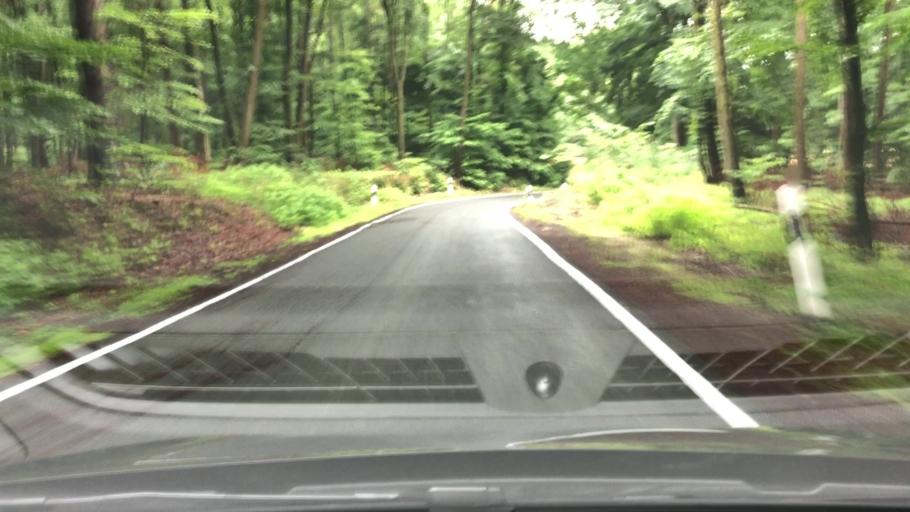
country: DE
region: North Rhine-Westphalia
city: Porta Westfalica
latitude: 52.2384
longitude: 8.9504
